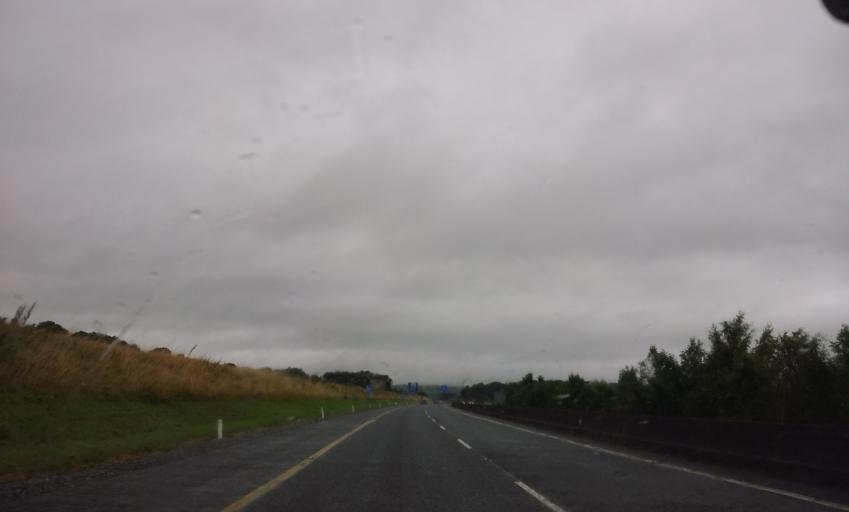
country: IE
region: Munster
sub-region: County Cork
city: Fermoy
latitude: 52.1524
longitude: -8.2664
